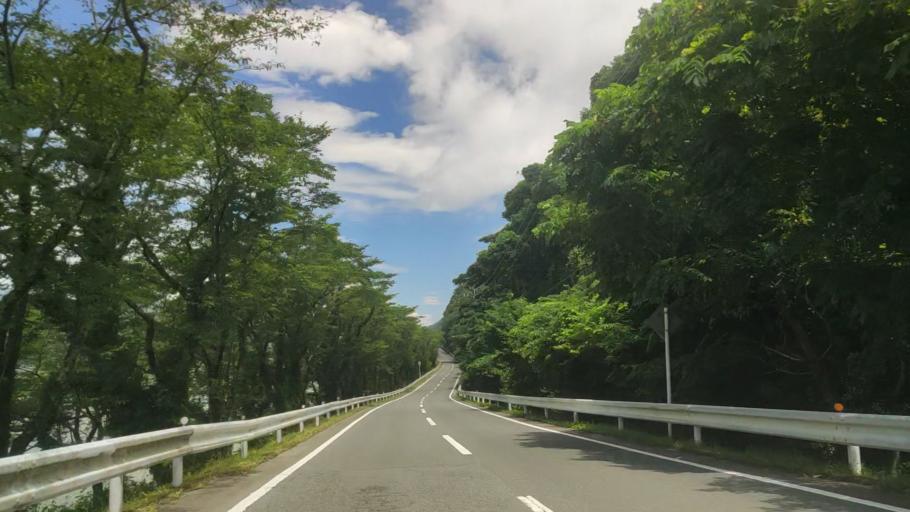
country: JP
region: Shizuoka
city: Fujinomiya
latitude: 35.2962
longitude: 138.4564
